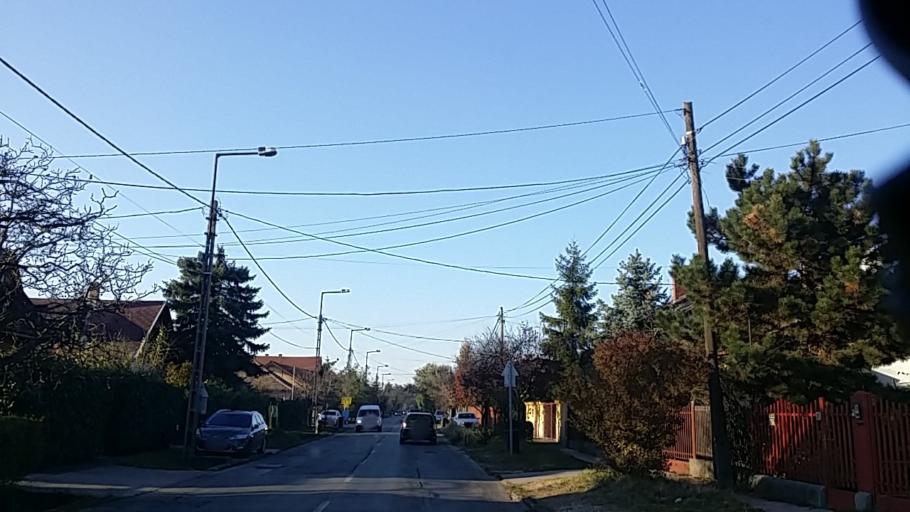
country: HU
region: Budapest
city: Budapest XVI. keruelet
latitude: 47.5041
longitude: 19.2134
